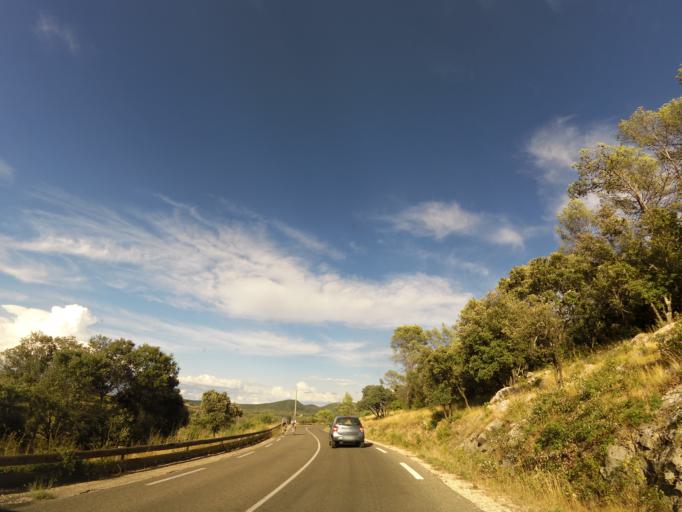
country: FR
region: Languedoc-Roussillon
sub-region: Departement de l'Herault
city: Saint-Drezery
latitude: 43.7807
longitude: 3.9287
